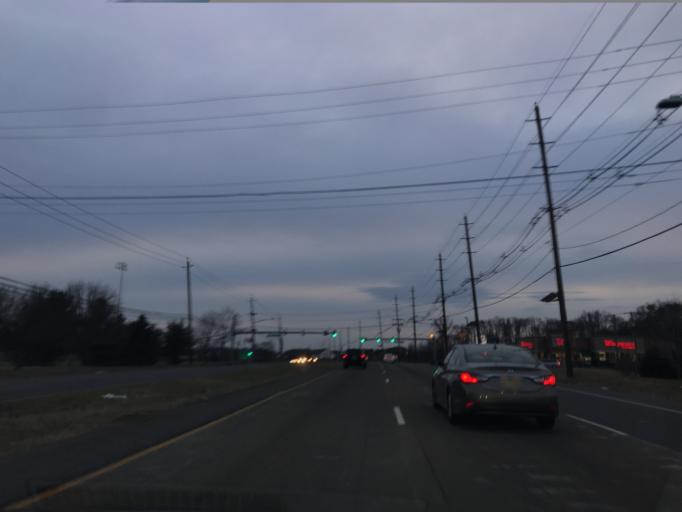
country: US
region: New Jersey
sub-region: Middlesex County
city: Milltown
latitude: 40.4293
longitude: -74.4927
